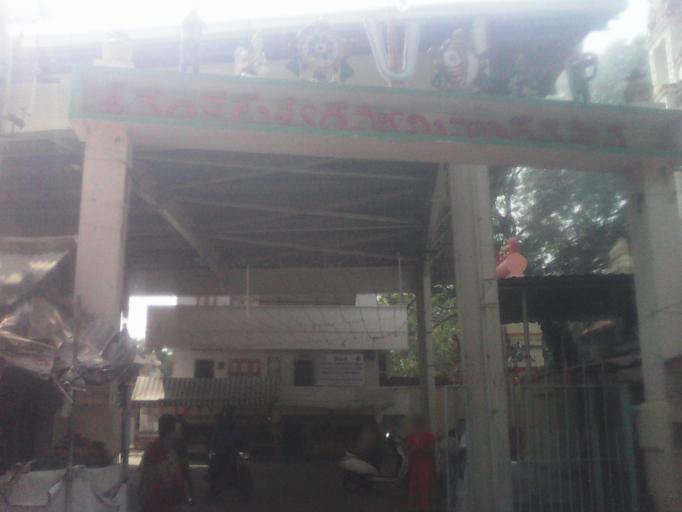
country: IN
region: Andhra Pradesh
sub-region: Krishna
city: Vijayawada
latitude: 16.5003
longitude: 80.6385
